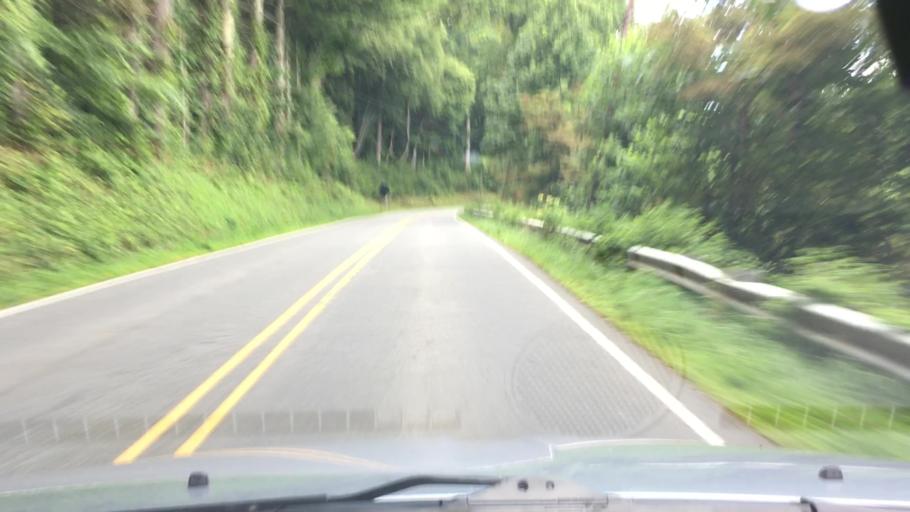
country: US
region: North Carolina
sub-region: Yancey County
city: Burnsville
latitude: 35.8631
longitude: -82.2002
